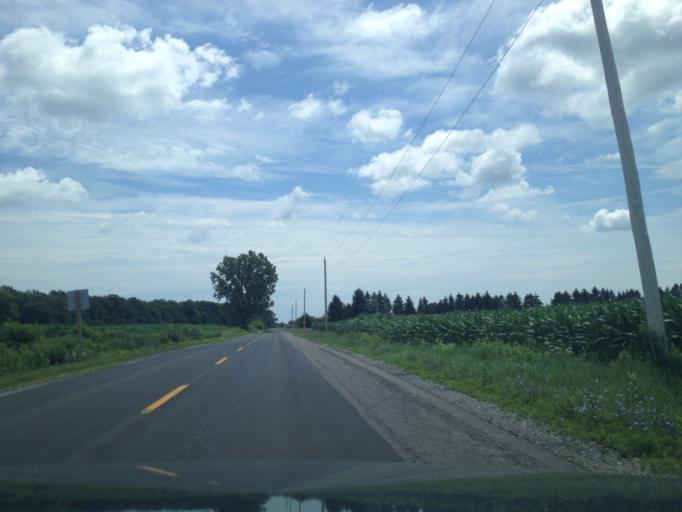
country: CA
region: Ontario
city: Norfolk County
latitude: 42.7930
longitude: -80.3075
